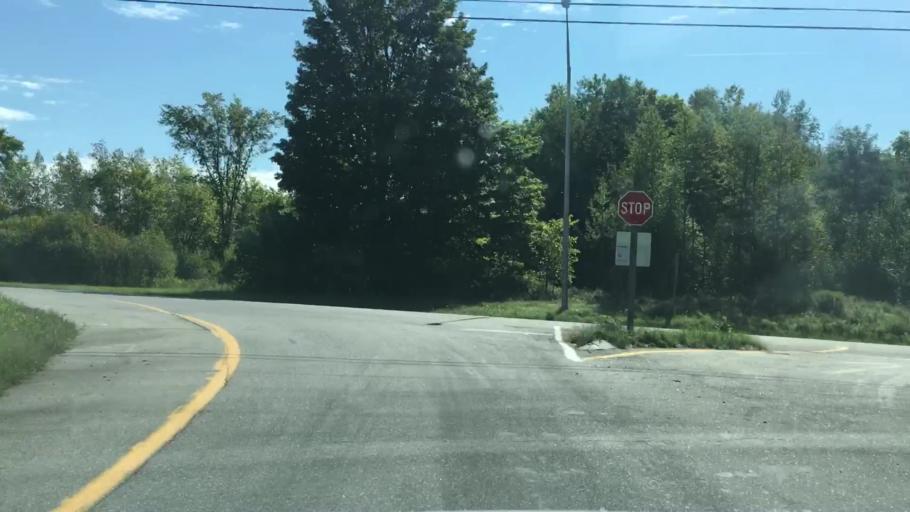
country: US
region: Maine
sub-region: Penobscot County
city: Newport
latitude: 44.8325
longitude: -69.2938
